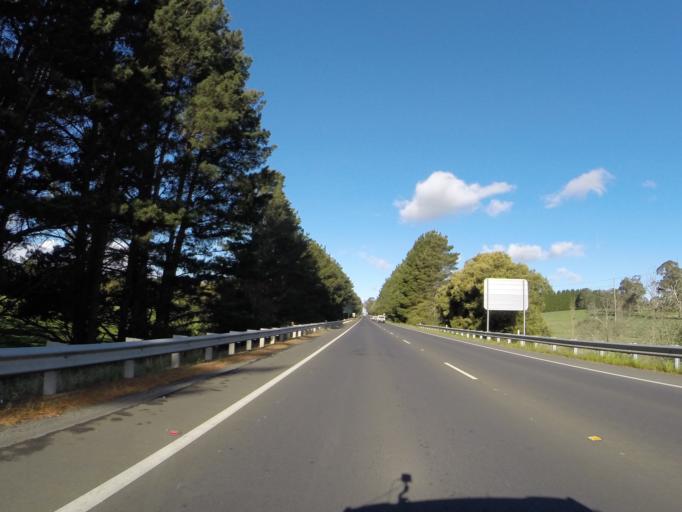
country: AU
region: New South Wales
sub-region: Wingecarribee
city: Moss Vale
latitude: -34.5755
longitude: 150.4811
